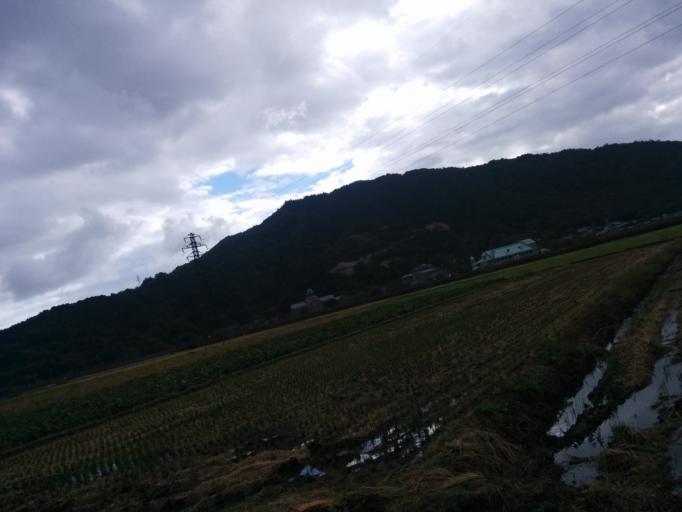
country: JP
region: Shiga Prefecture
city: Omihachiman
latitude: 35.1505
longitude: 136.1394
